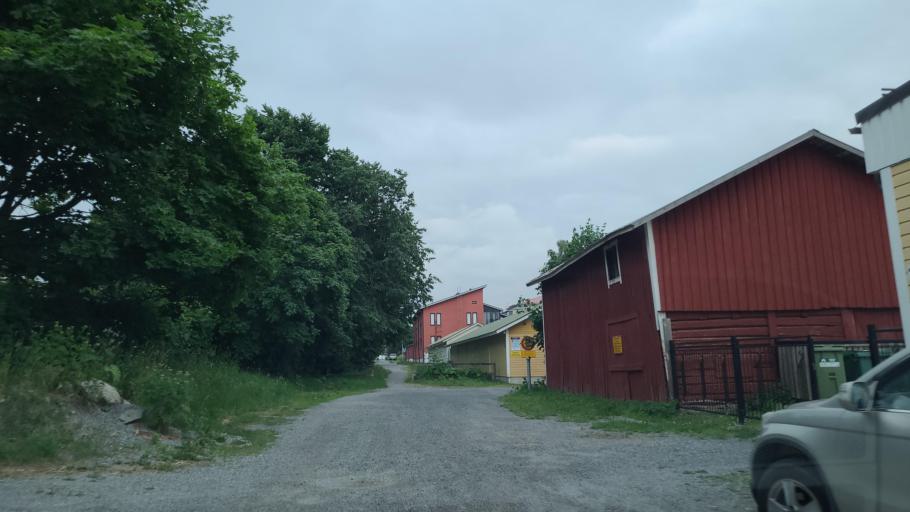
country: FI
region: Ostrobothnia
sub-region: Vaasa
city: Vaasa
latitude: 63.1031
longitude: 21.6175
